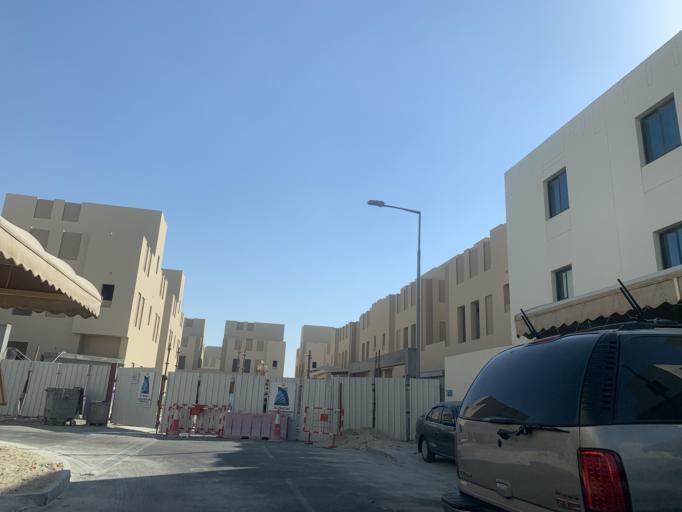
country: BH
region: Central Governorate
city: Madinat Hamad
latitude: 26.1228
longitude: 50.4818
